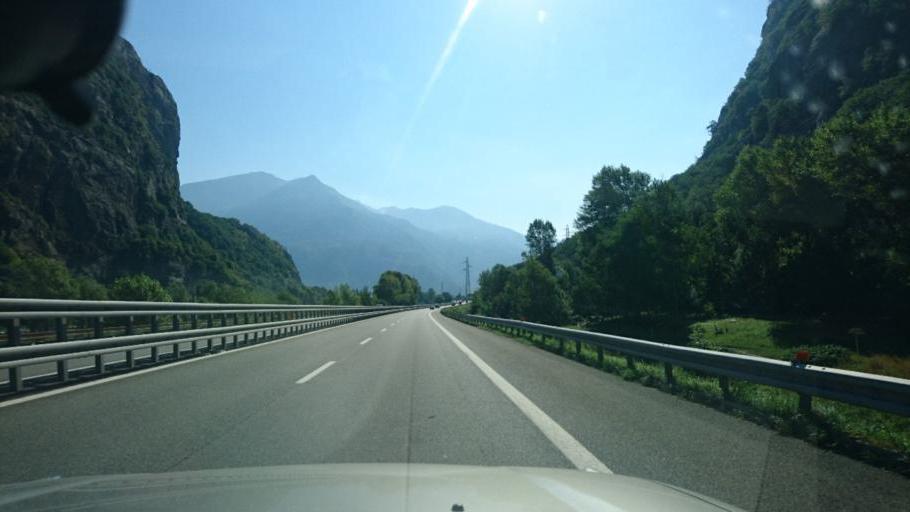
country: IT
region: Aosta Valley
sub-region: Valle d'Aosta
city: Bard
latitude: 45.6033
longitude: 7.7467
